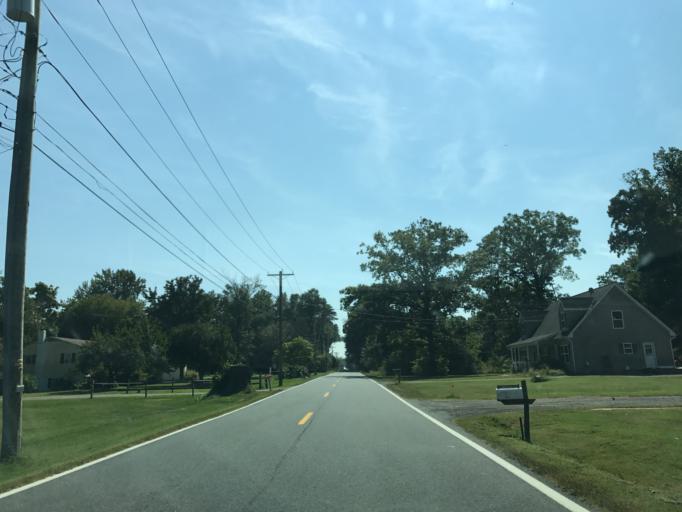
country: US
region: Maryland
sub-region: Cecil County
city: Elkton
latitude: 39.5146
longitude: -75.8131
